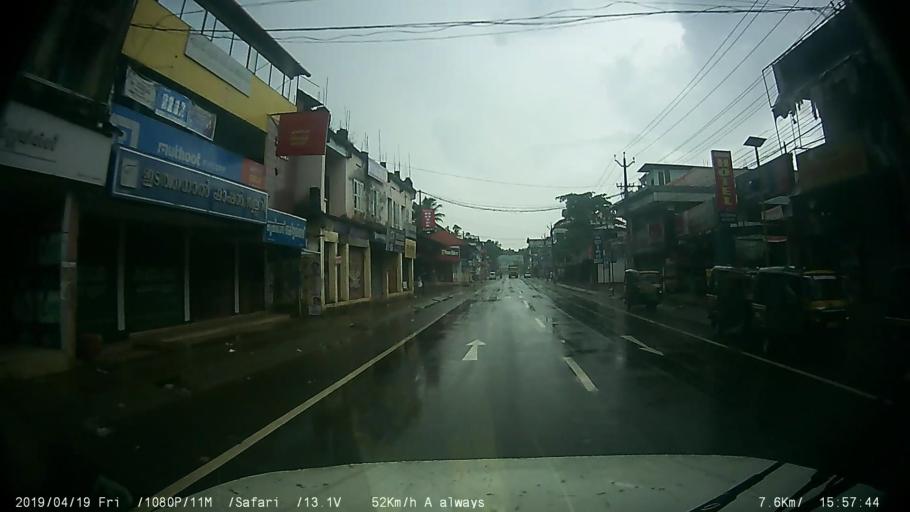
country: IN
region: Kerala
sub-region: Kottayam
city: Palackattumala
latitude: 9.7542
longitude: 76.5610
